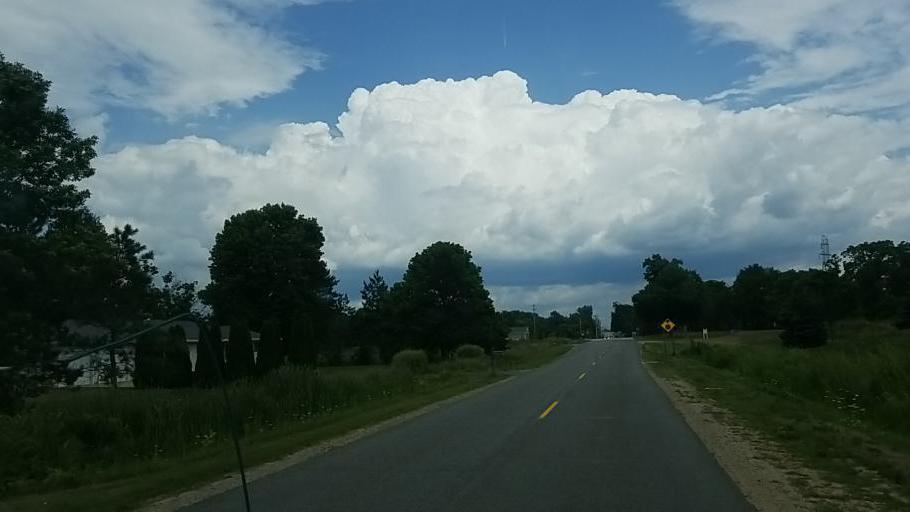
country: US
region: Michigan
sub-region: Kent County
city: Walker
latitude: 43.0161
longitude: -85.7904
